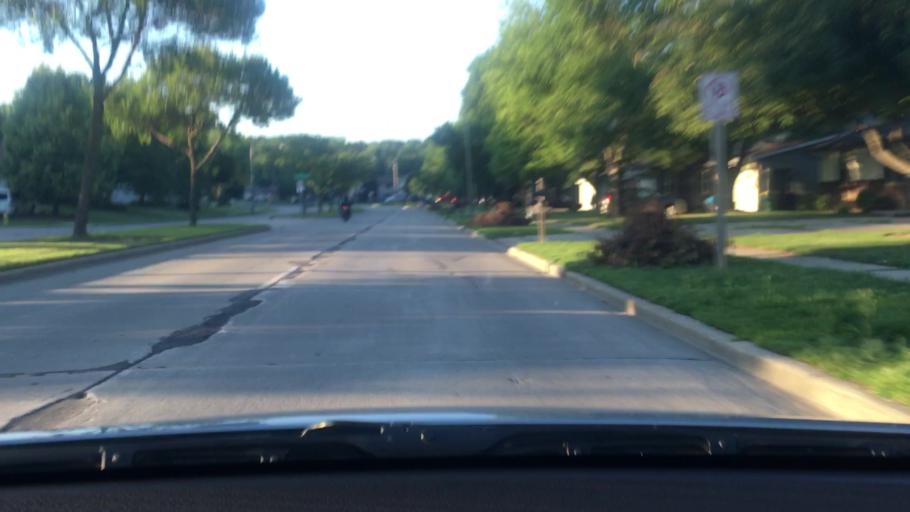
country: US
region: Wisconsin
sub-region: Brown County
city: Ashwaubenon
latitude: 44.5036
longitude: -88.1002
